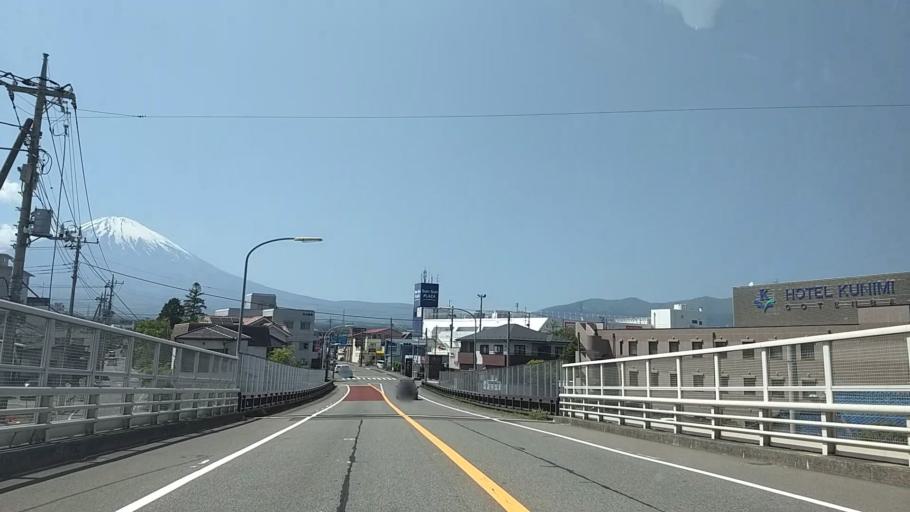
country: JP
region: Shizuoka
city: Gotemba
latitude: 35.3034
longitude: 138.9358
